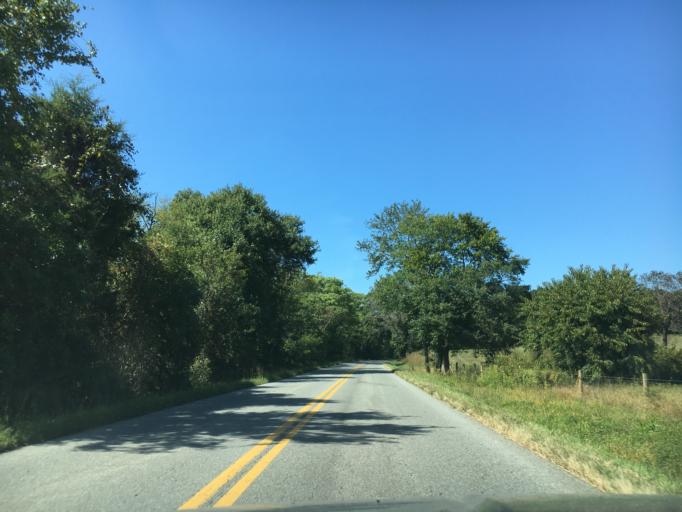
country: US
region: Virginia
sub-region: Albemarle County
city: Crozet
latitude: 37.9587
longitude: -78.6633
